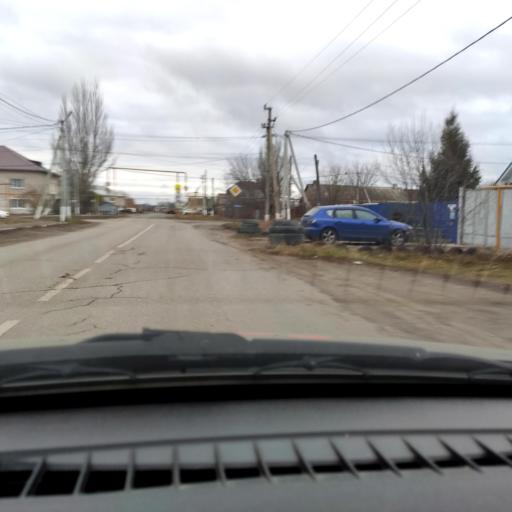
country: RU
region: Samara
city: Podstepki
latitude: 53.5165
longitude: 49.1182
